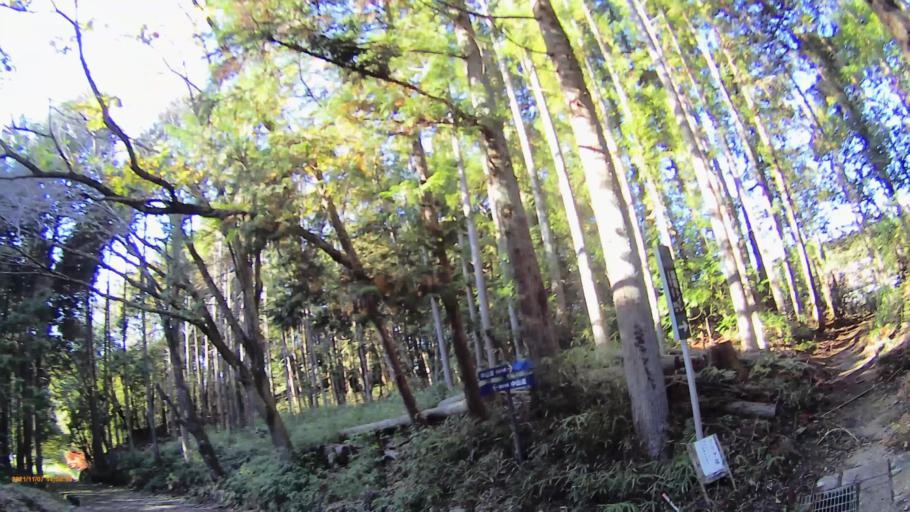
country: JP
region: Gifu
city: Mitake
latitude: 35.4349
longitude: 137.1717
